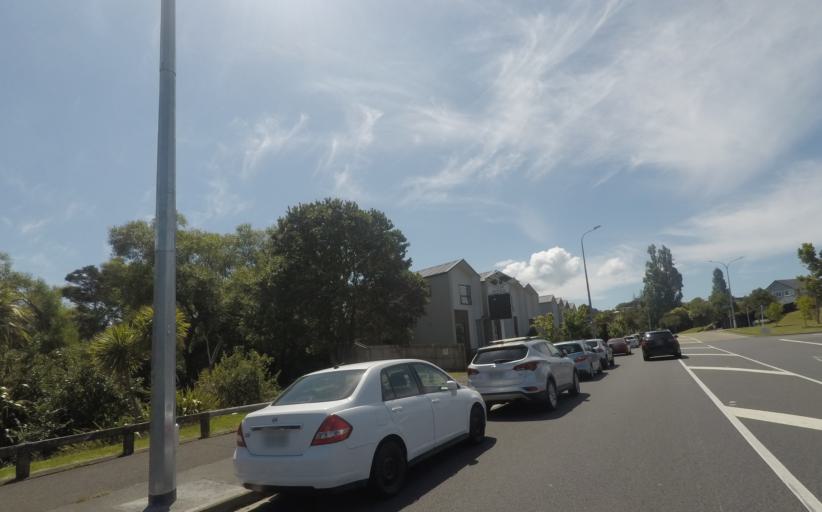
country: NZ
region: Auckland
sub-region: Auckland
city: Tamaki
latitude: -36.8727
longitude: 174.8531
